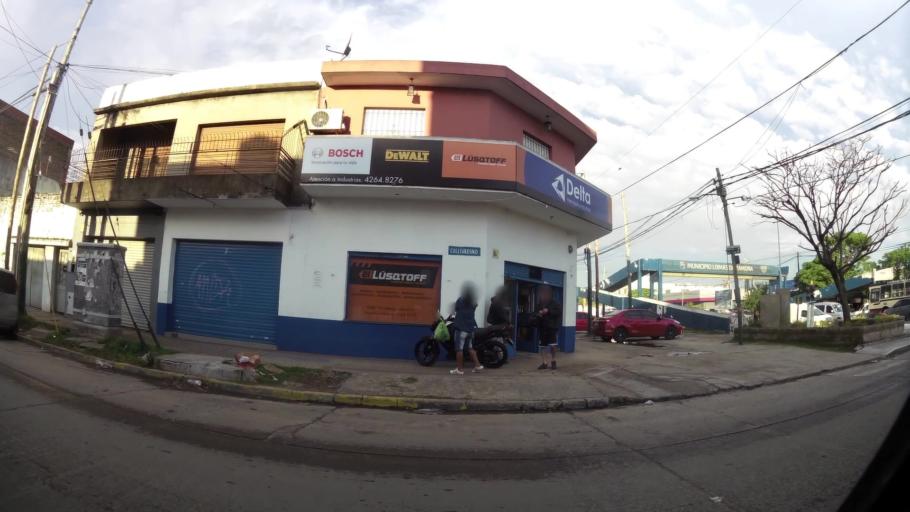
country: AR
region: Buenos Aires
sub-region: Partido de Lomas de Zamora
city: Lomas de Zamora
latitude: -34.7615
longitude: -58.3622
